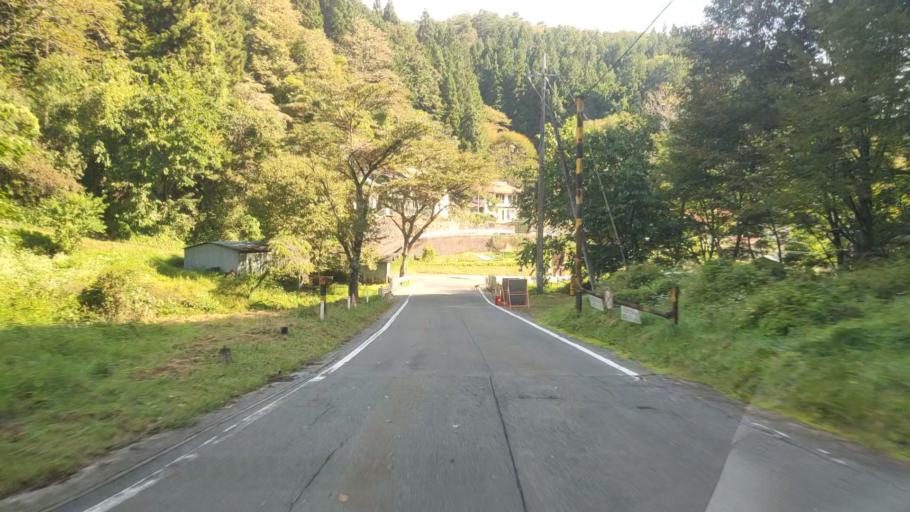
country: JP
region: Gunma
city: Nakanojomachi
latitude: 36.5996
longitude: 138.7048
